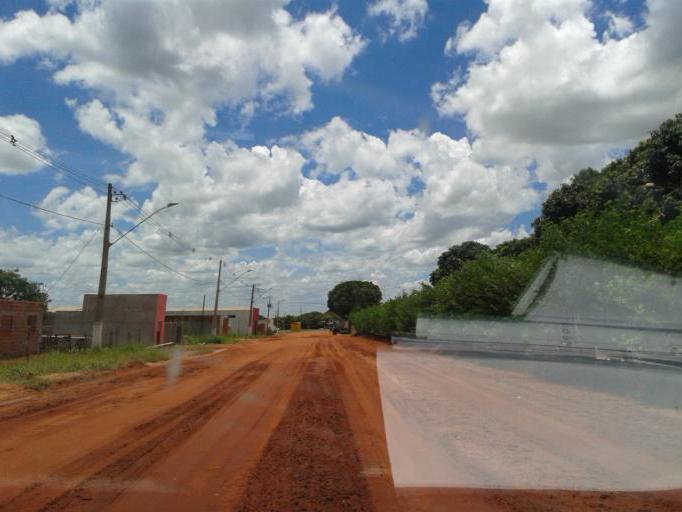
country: BR
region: Minas Gerais
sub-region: Santa Vitoria
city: Santa Vitoria
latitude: -18.8560
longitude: -50.1319
